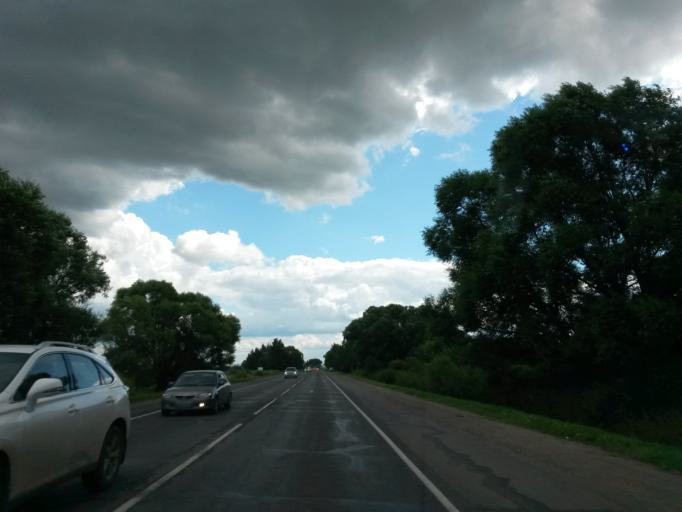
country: RU
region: Jaroslavl
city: Yaroslavl
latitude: 57.5615
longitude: 39.8432
